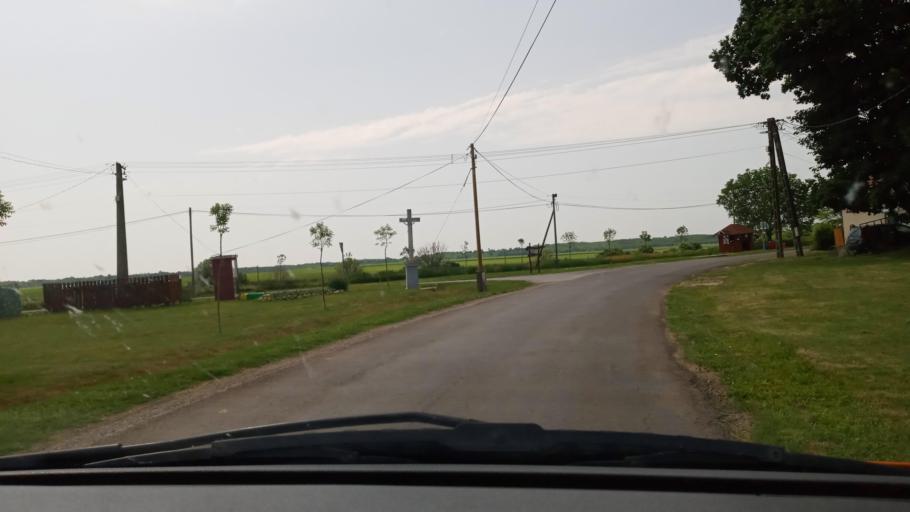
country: HU
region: Baranya
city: Szentlorinc
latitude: 45.9926
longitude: 18.0343
